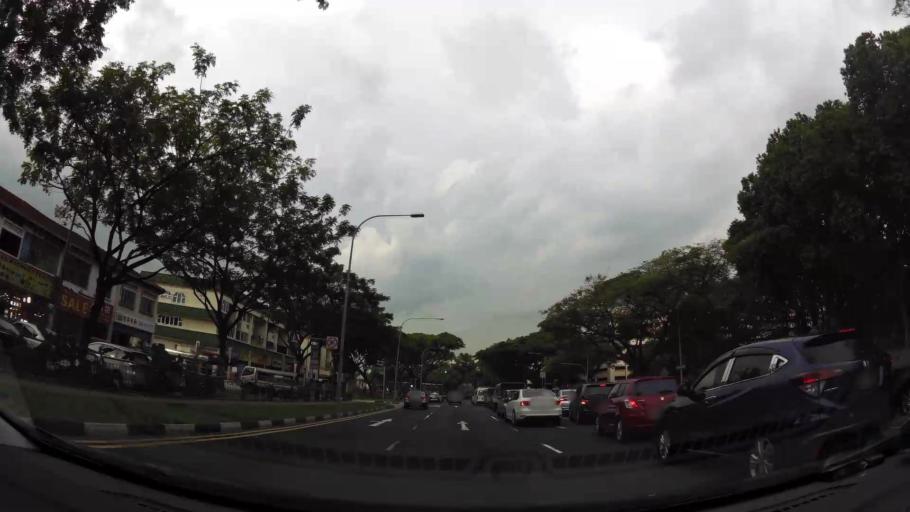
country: MY
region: Johor
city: Kampung Pasir Gudang Baru
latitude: 1.4258
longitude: 103.8260
